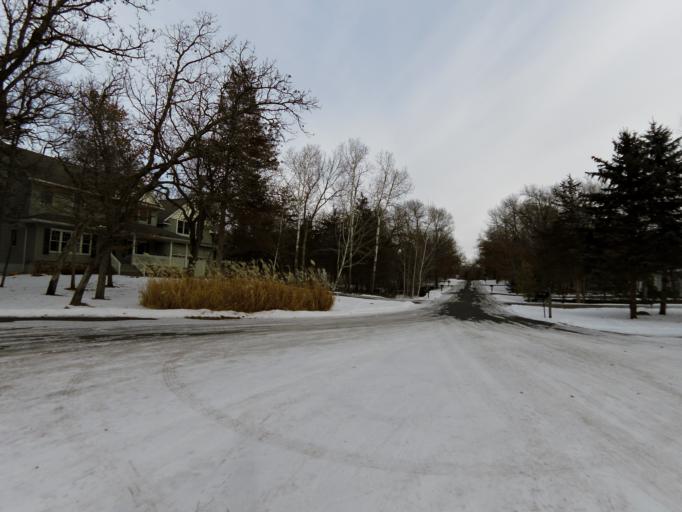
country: US
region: Minnesota
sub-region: Washington County
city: Afton
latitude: 44.9110
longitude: -92.7751
